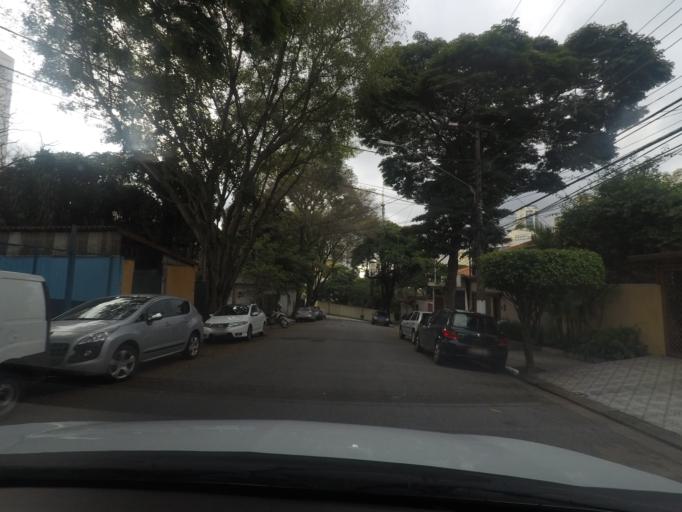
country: BR
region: Sao Paulo
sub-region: Diadema
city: Diadema
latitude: -23.6504
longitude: -46.6674
